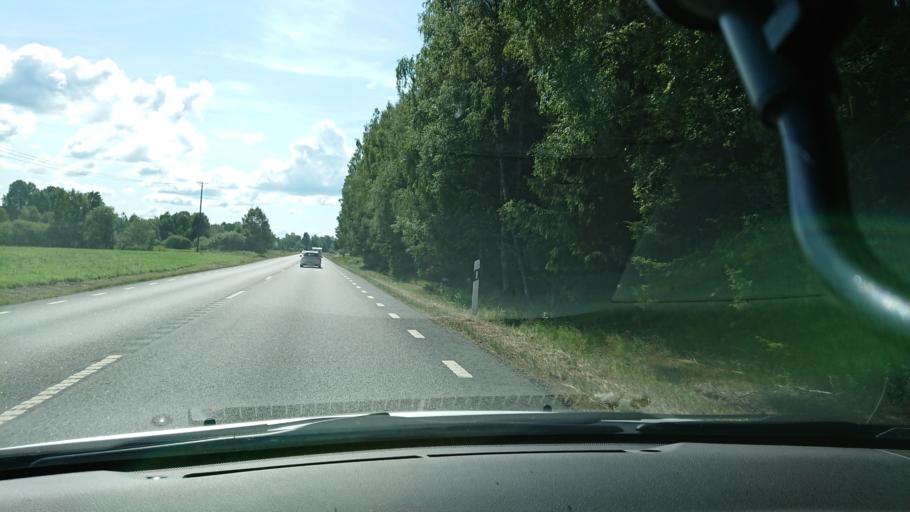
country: SE
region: OEstergoetland
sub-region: Kinda Kommun
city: Kisa
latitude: 57.8961
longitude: 15.7128
